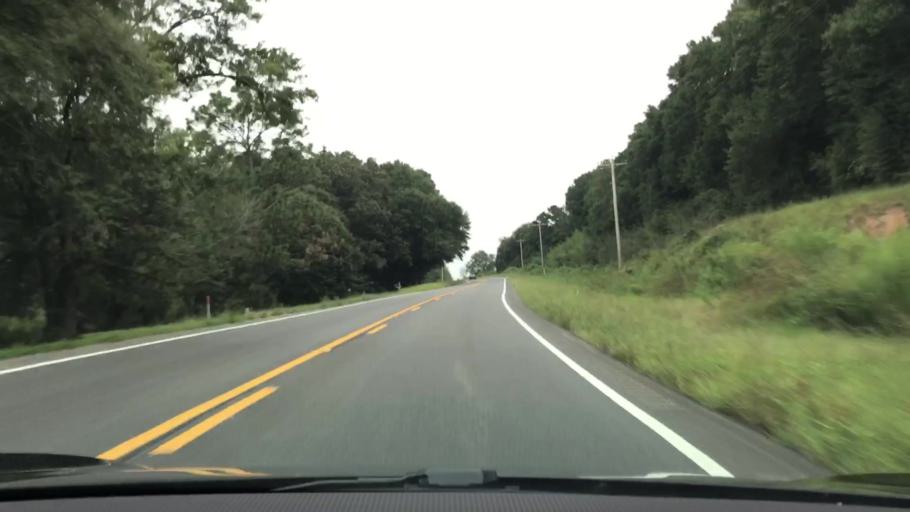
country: US
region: Alabama
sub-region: Covington County
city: Opp
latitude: 31.2288
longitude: -86.1620
